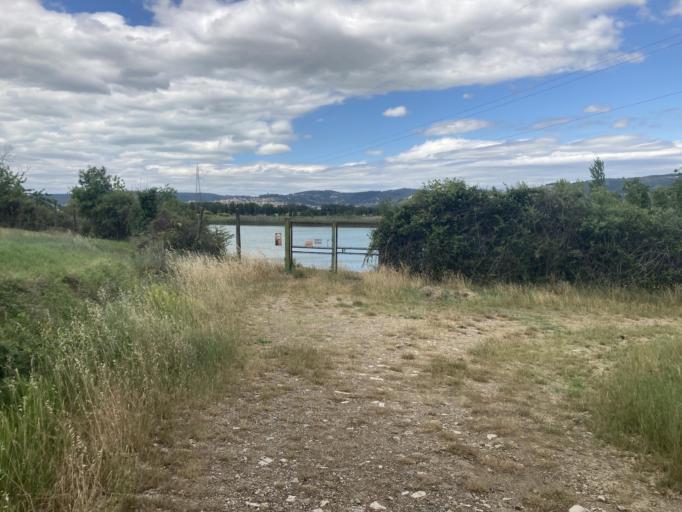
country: IT
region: Umbria
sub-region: Provincia di Perugia
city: Corciano
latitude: 43.1257
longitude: 12.2599
